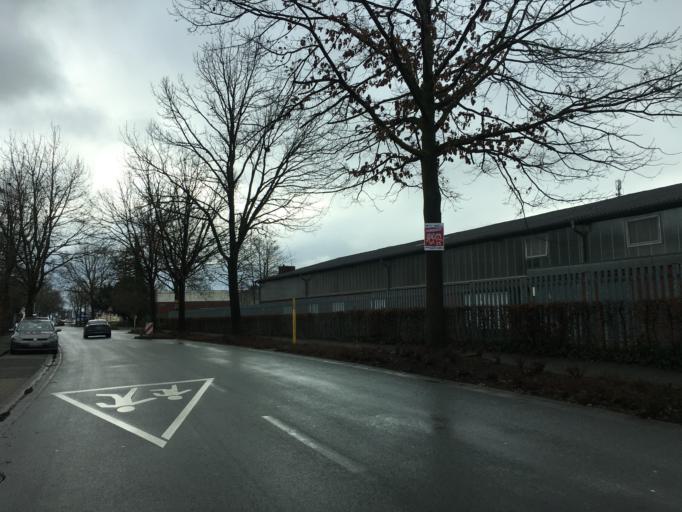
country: DE
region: North Rhine-Westphalia
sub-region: Regierungsbezirk Munster
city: Senden
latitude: 51.9137
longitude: 7.4816
